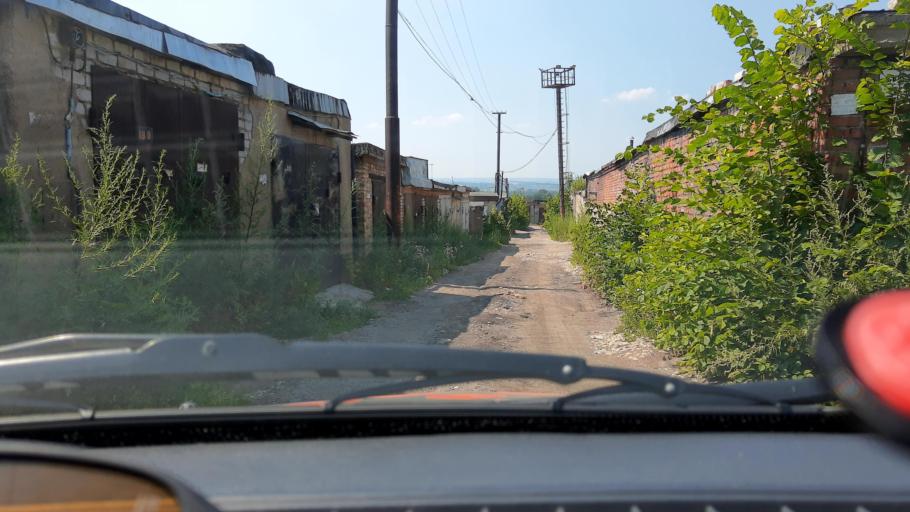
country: RU
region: Bashkortostan
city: Ufa
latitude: 54.8266
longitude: 56.0811
